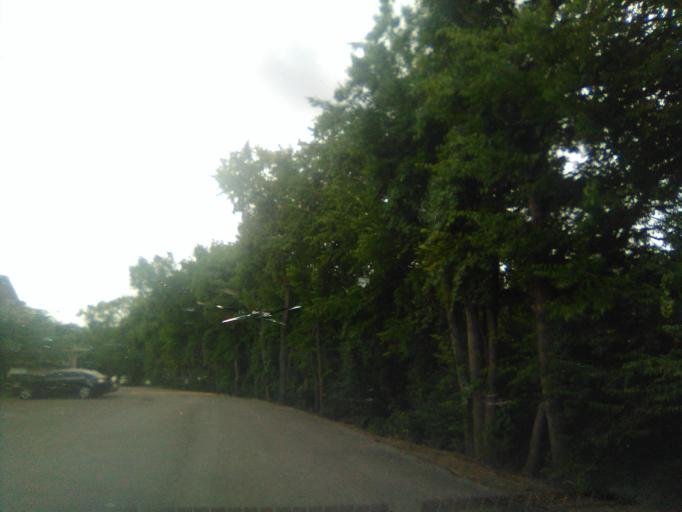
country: US
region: Tennessee
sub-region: Davidson County
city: Belle Meade
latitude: 36.0877
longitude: -86.8925
